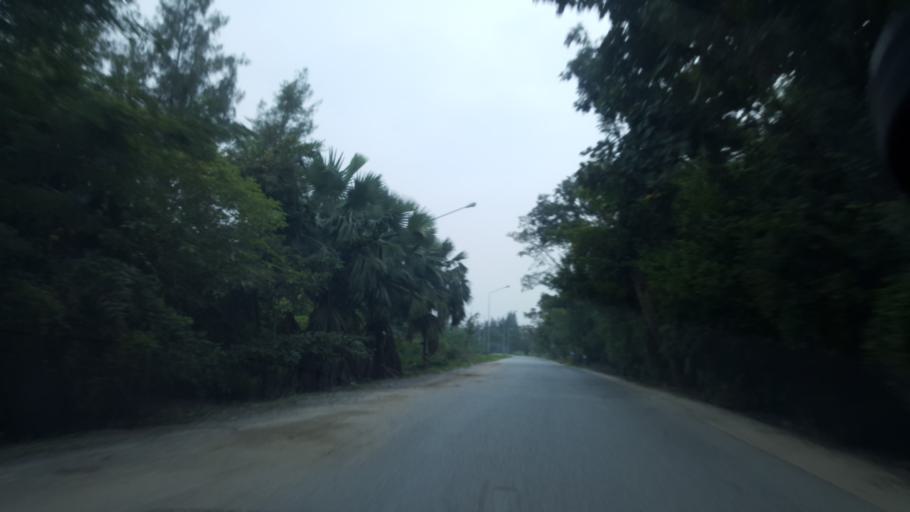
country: TH
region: Chon Buri
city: Si Racha
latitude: 13.2372
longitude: 101.0196
